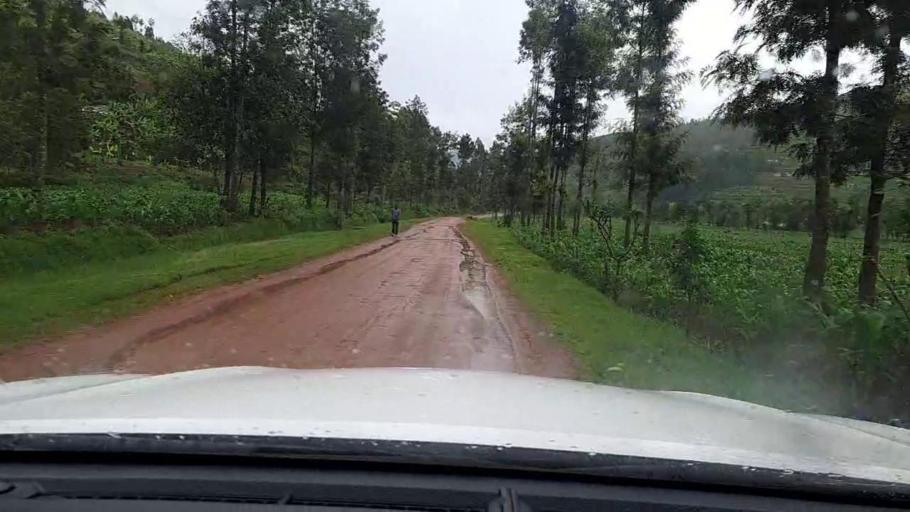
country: RW
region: Northern Province
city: Byumba
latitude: -1.7362
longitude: 29.9412
